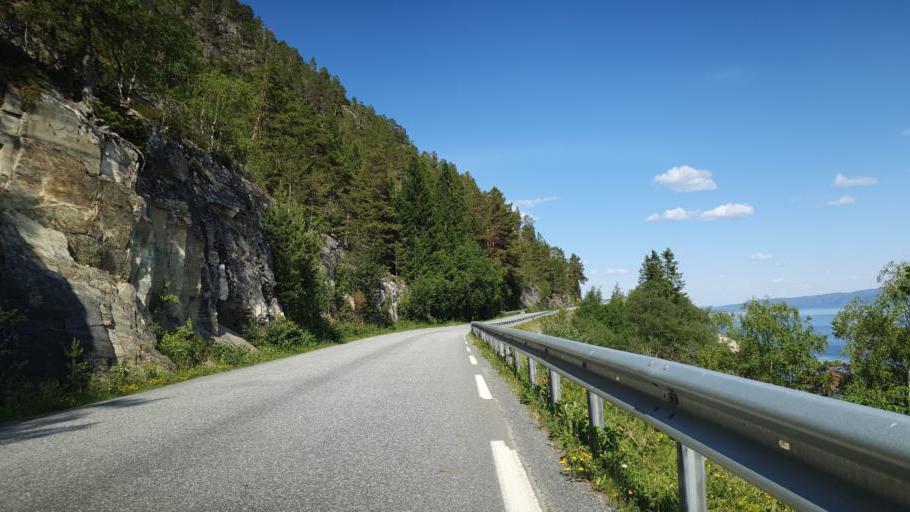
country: NO
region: Nord-Trondelag
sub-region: Leksvik
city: Leksvik
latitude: 63.6278
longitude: 10.5616
